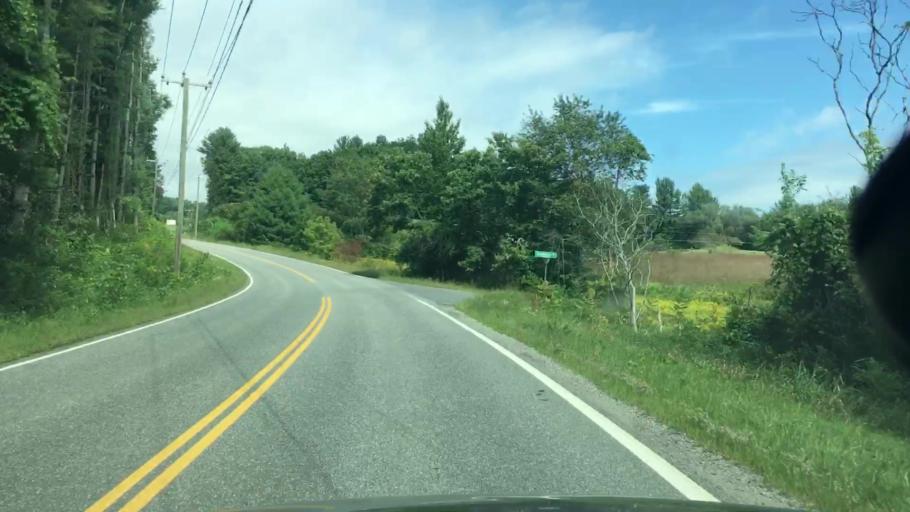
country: US
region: Massachusetts
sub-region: Franklin County
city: Colrain
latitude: 42.6385
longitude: -72.6692
